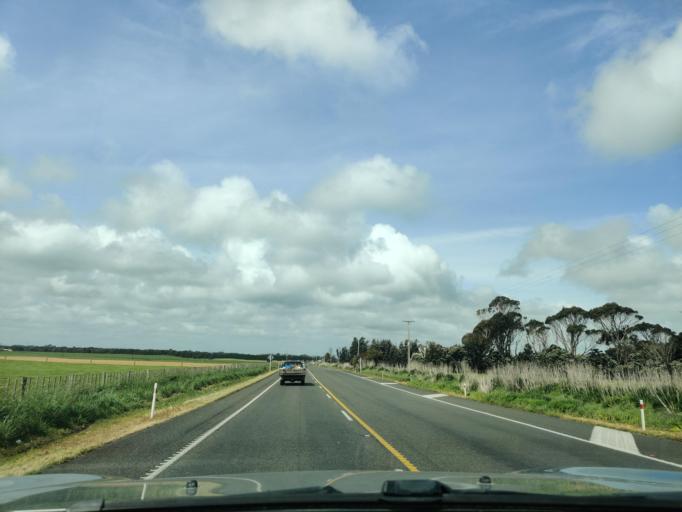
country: NZ
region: Taranaki
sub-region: South Taranaki District
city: Patea
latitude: -39.7671
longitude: 174.6071
